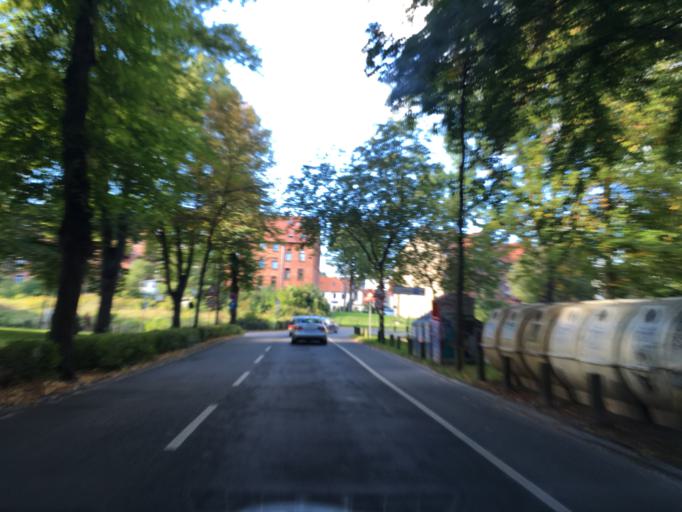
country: DE
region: Lower Saxony
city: Lueneburg
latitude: 53.2519
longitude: 10.4029
